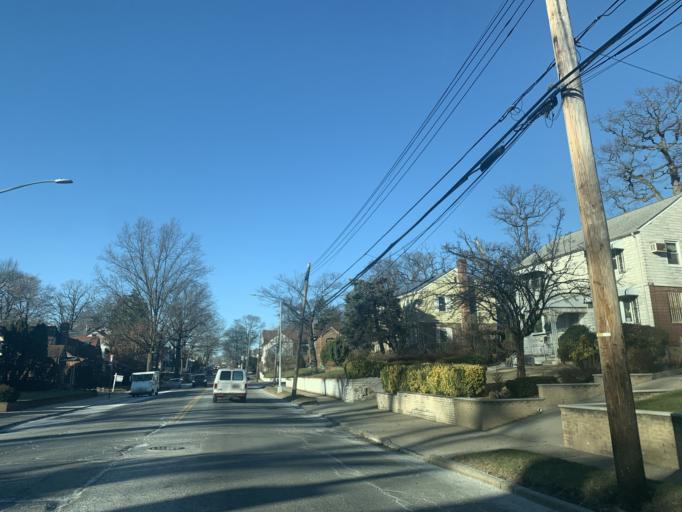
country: US
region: New York
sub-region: Queens County
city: Jamaica
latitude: 40.7177
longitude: -73.7748
